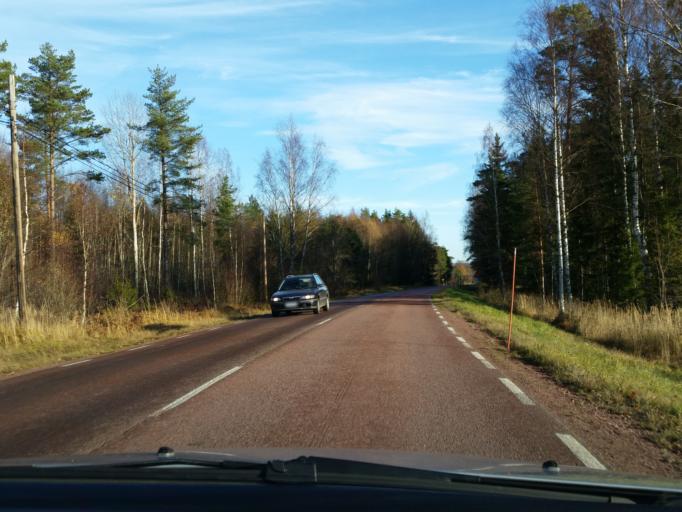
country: AX
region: Alands landsbygd
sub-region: Finstroem
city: Finstroem
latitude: 60.3067
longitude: 19.9592
